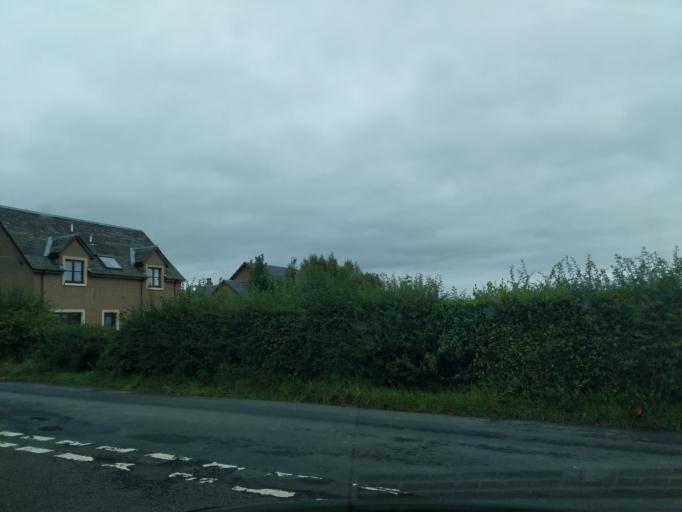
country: GB
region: Scotland
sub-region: The Scottish Borders
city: Saint Boswells
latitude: 55.5713
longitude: -2.6382
